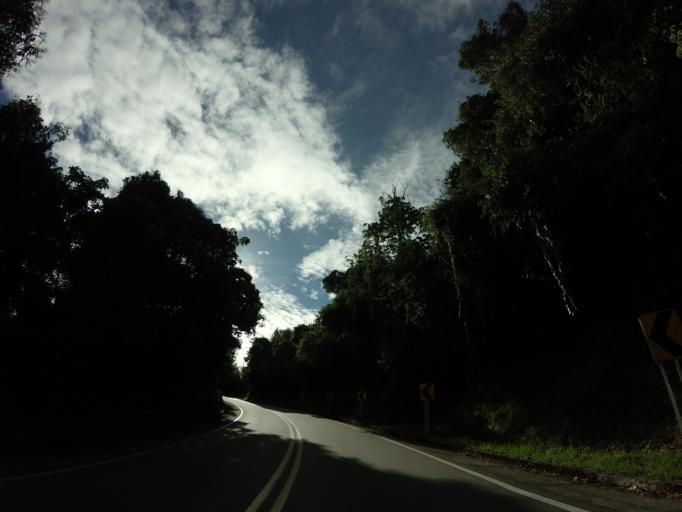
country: CO
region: Tolima
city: Herveo
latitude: 5.1384
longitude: -75.1772
